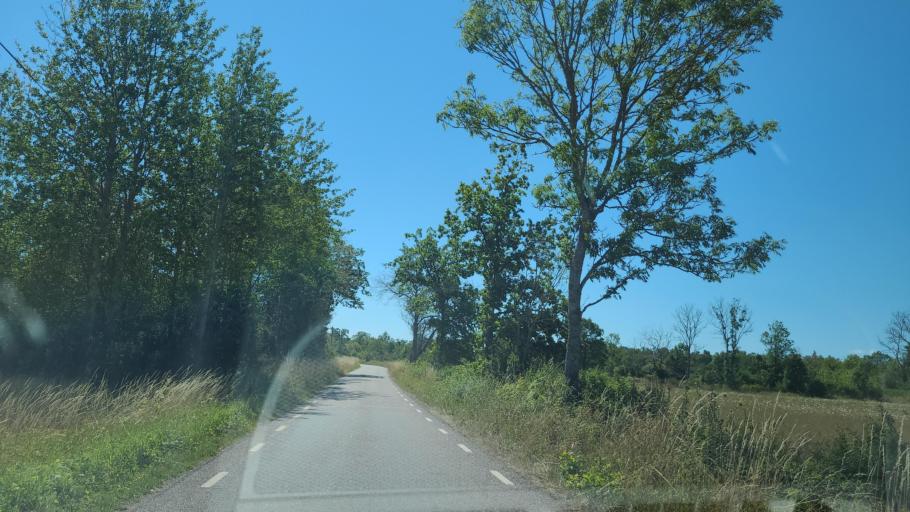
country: SE
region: Kalmar
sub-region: Borgholms Kommun
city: Borgholm
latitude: 56.7652
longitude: 16.6504
